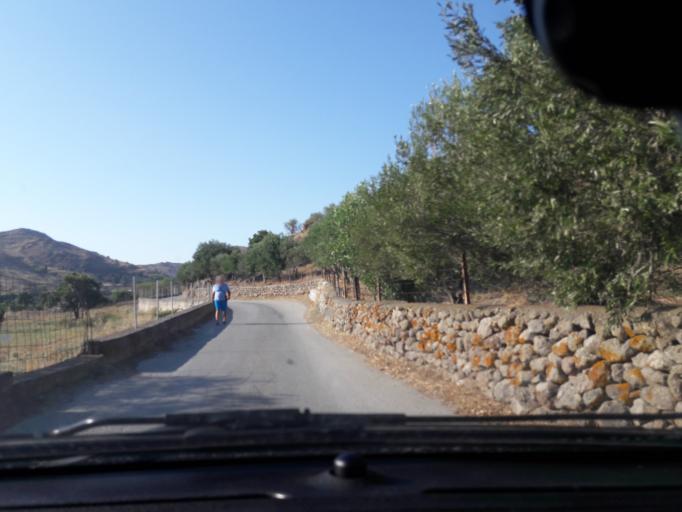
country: GR
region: North Aegean
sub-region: Nomos Lesvou
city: Myrina
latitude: 39.8473
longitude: 25.0850
